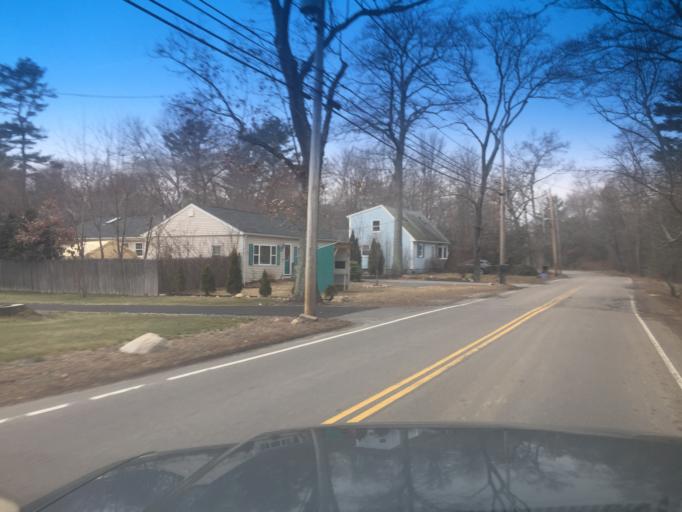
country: US
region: Massachusetts
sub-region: Norfolk County
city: Bellingham
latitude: 42.1157
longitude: -71.4495
